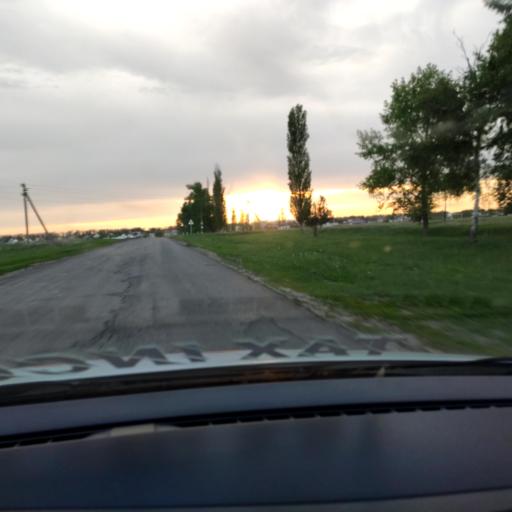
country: RU
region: Voronezj
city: Maslovka
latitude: 51.4458
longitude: 39.2502
